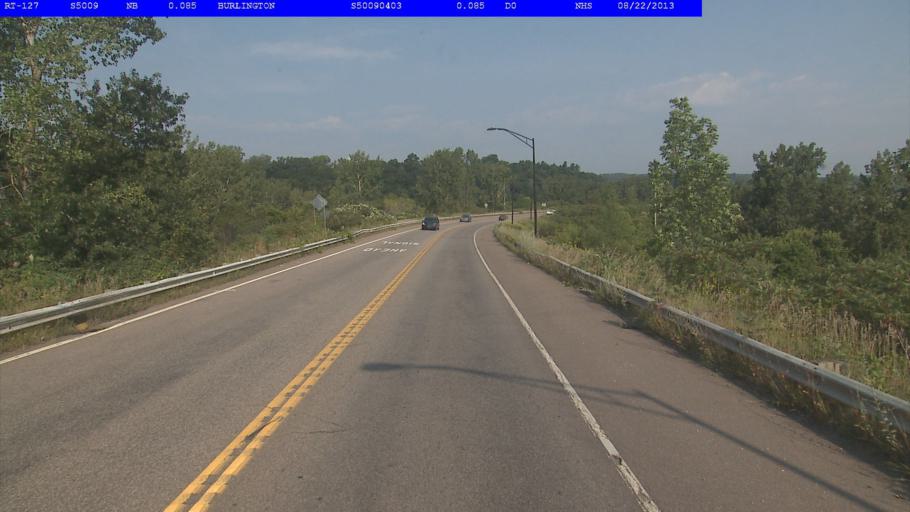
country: US
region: Vermont
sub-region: Chittenden County
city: Burlington
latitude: 44.4883
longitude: -73.2204
